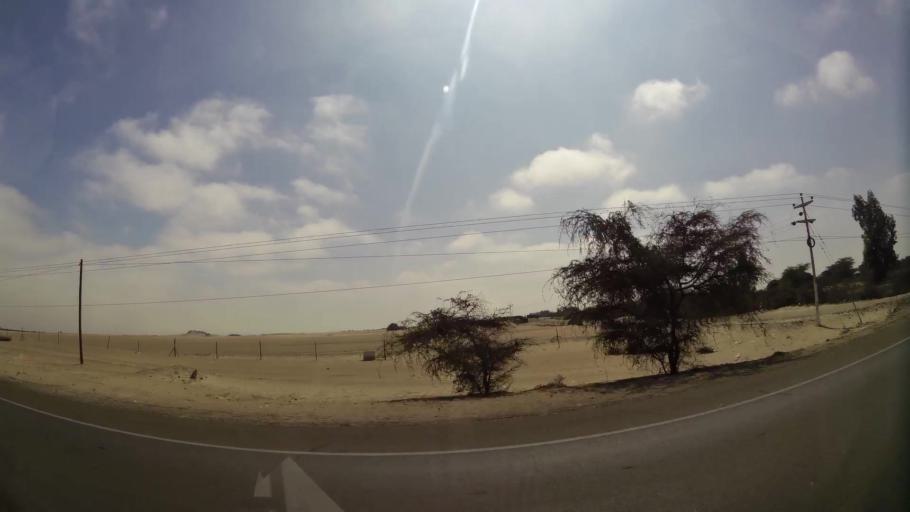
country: PE
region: Ica
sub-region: Provincia de Ica
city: Guadalupe
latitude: -13.9251
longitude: -75.9868
